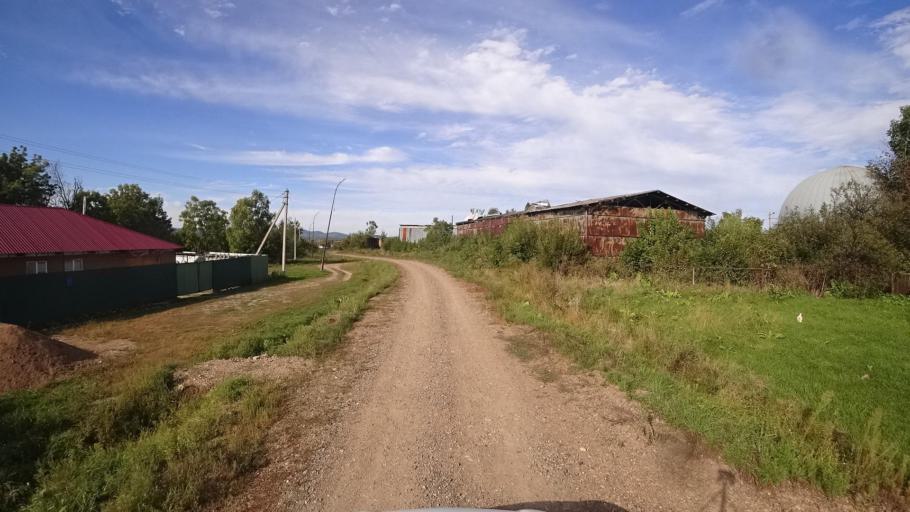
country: RU
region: Primorskiy
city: Dostoyevka
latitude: 44.3010
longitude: 133.4550
